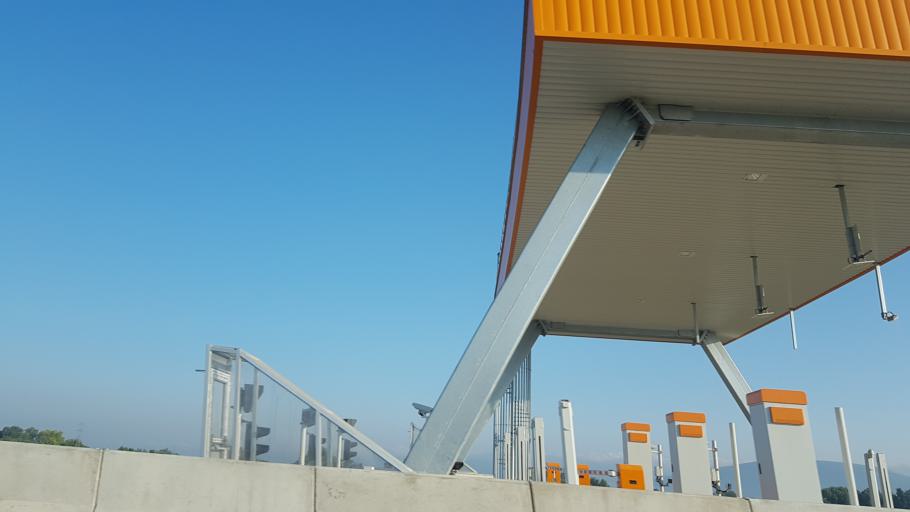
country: TR
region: Bursa
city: Karacabey
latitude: 40.1903
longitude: 28.3426
